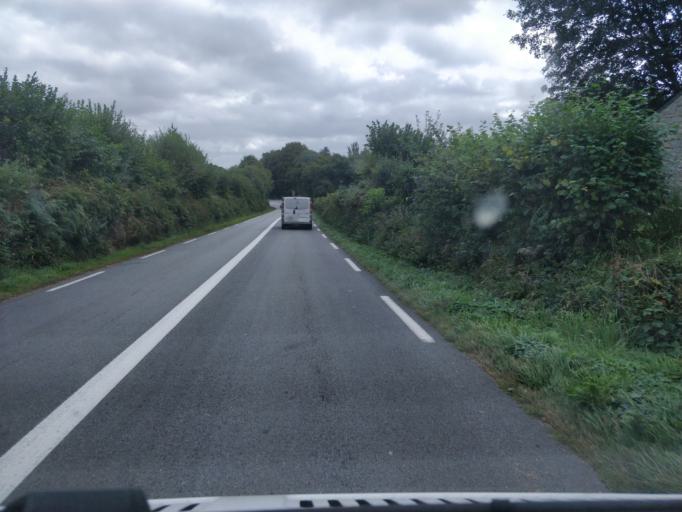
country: FR
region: Brittany
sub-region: Departement du Finistere
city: Pluguffan
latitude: 47.9994
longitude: -4.1670
